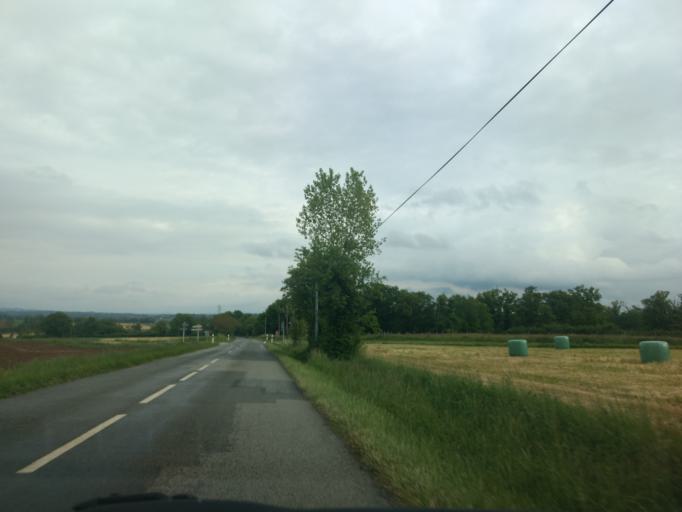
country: FR
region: Midi-Pyrenees
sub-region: Departement de l'Aveyron
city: Montbazens
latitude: 44.5030
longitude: 2.1971
